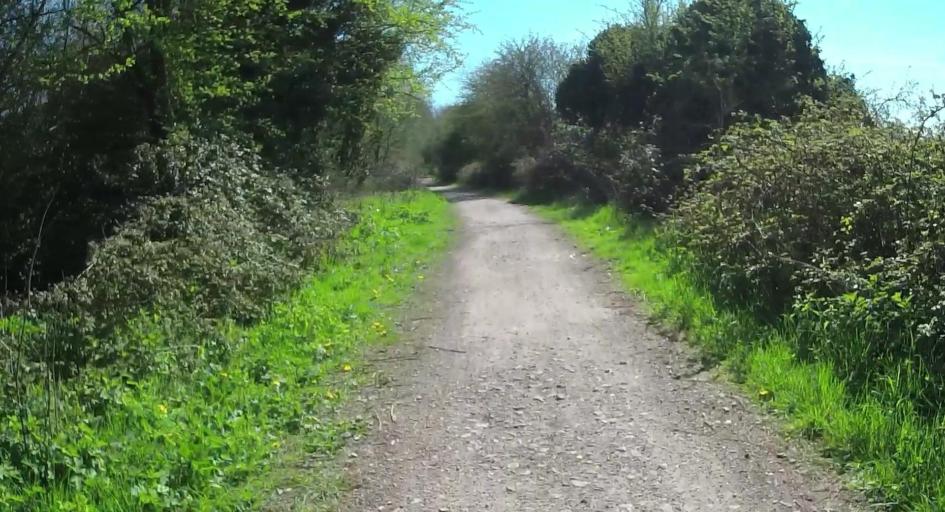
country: GB
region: England
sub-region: Hampshire
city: Romsey
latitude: 51.0608
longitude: -1.5148
